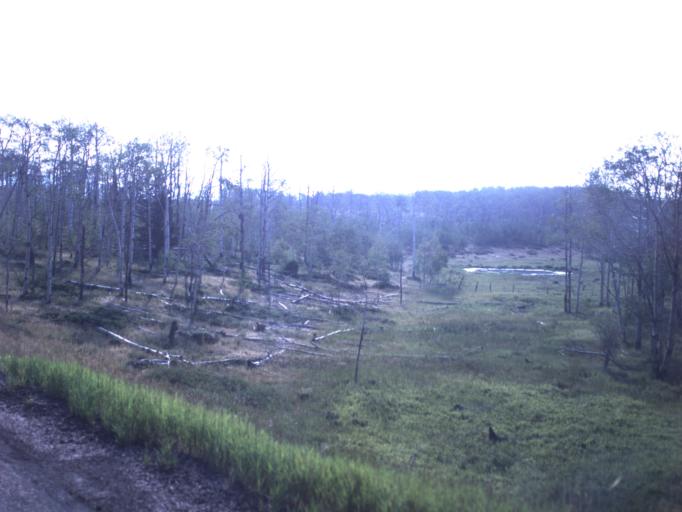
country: US
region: Utah
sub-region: Uintah County
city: Maeser
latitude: 40.7223
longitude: -109.4721
